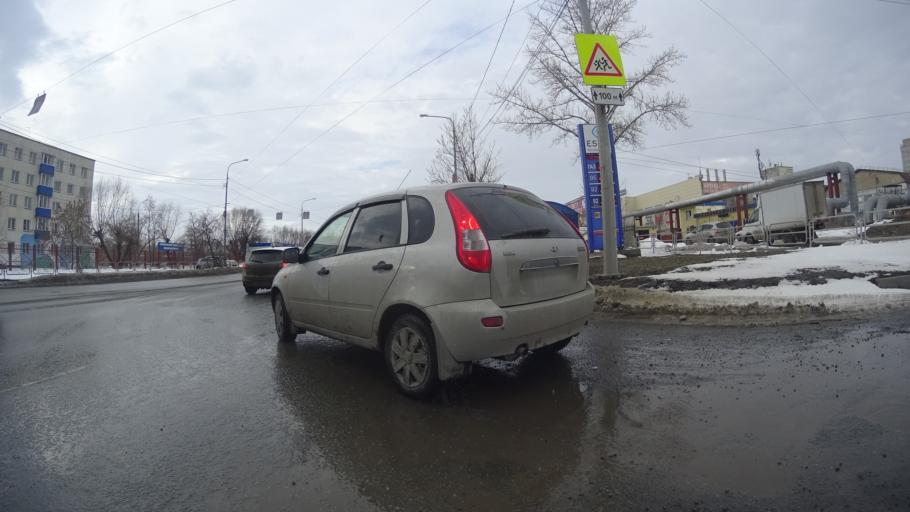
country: RU
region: Chelyabinsk
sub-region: Gorod Chelyabinsk
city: Chelyabinsk
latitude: 55.2024
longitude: 61.3264
